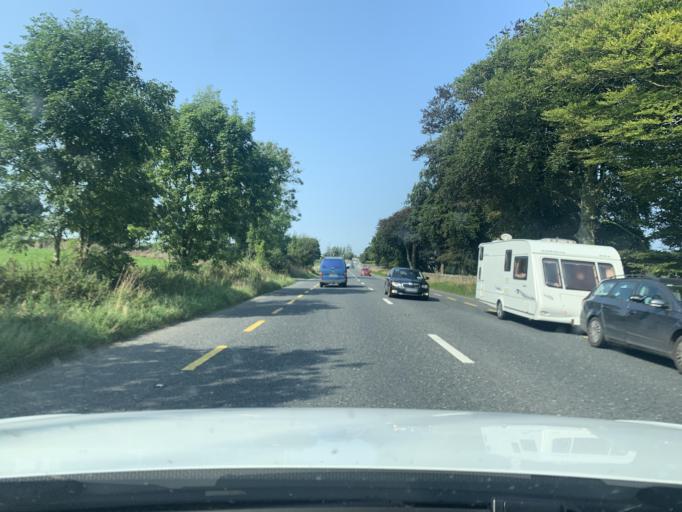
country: IE
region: Leinster
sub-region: An Iarmhi
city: Athlone
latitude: 53.5020
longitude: -8.0421
